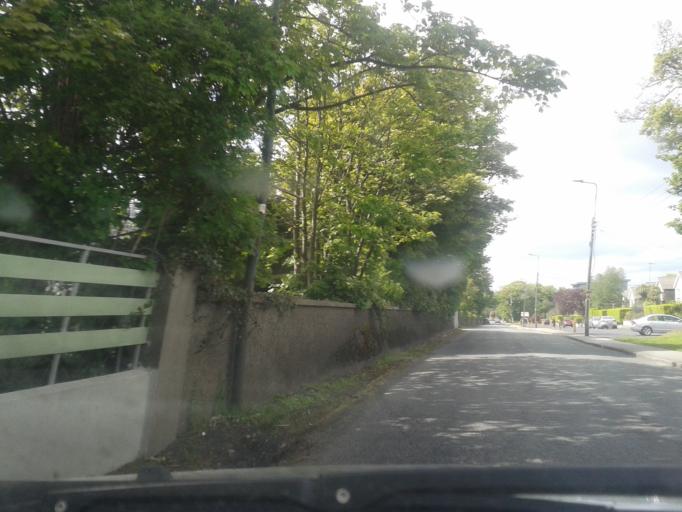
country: IE
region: Leinster
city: Cabinteely
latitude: 53.2761
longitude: -6.1518
